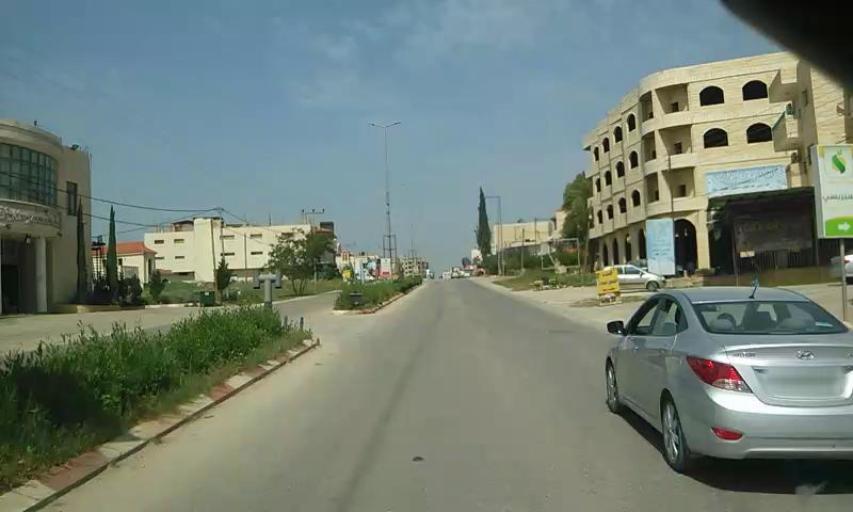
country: PS
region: West Bank
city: Janin
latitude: 32.4827
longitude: 35.2994
